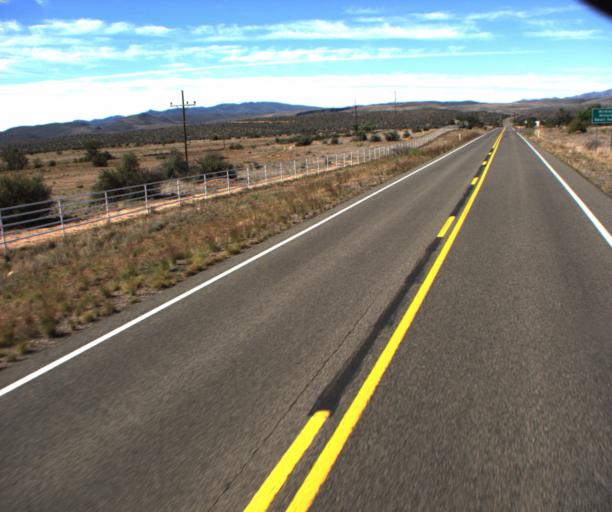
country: US
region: Arizona
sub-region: Yavapai County
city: Prescott
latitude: 34.3740
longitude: -112.6625
